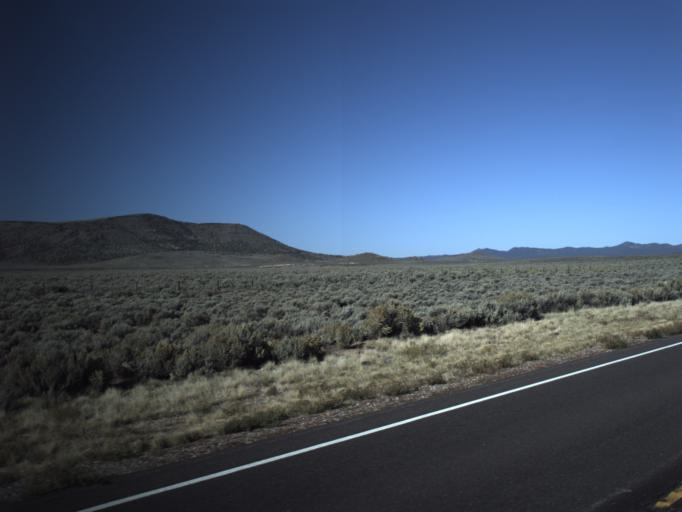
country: US
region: Utah
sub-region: Washington County
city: Enterprise
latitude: 37.7848
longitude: -113.8708
